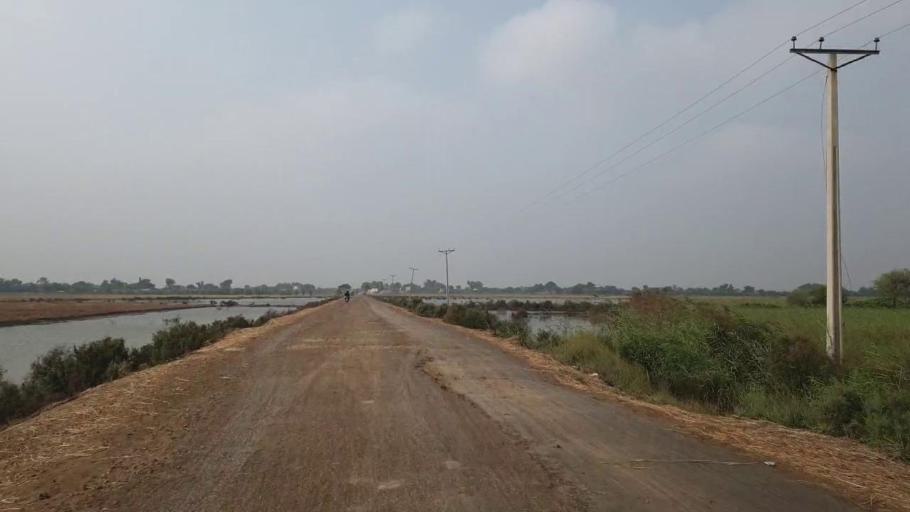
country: PK
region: Sindh
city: Matli
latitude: 24.9731
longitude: 68.6067
